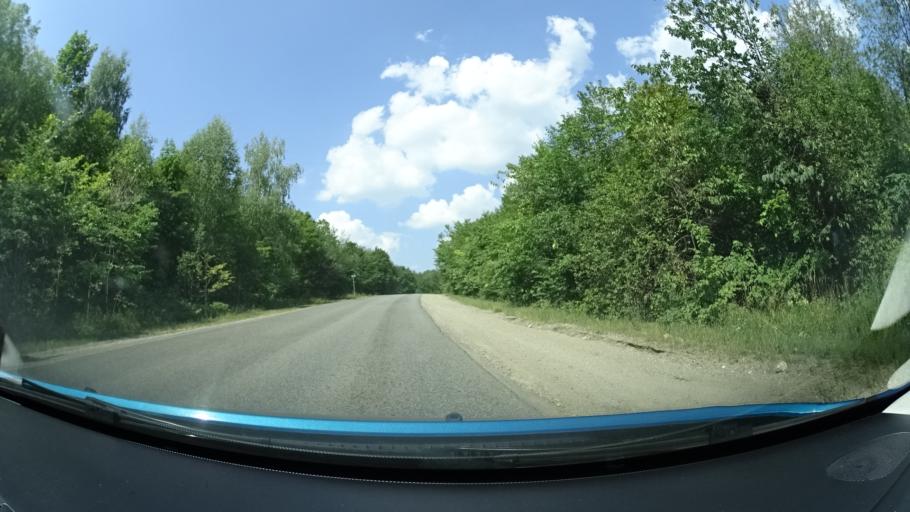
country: RU
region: Bashkortostan
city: Oktyabr'skiy
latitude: 54.4604
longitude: 53.5772
